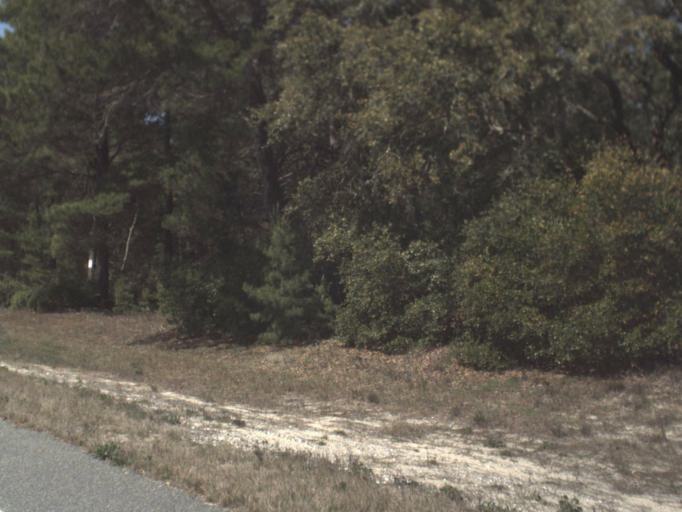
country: US
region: Florida
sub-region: Franklin County
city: Carrabelle
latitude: 29.9322
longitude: -84.4398
